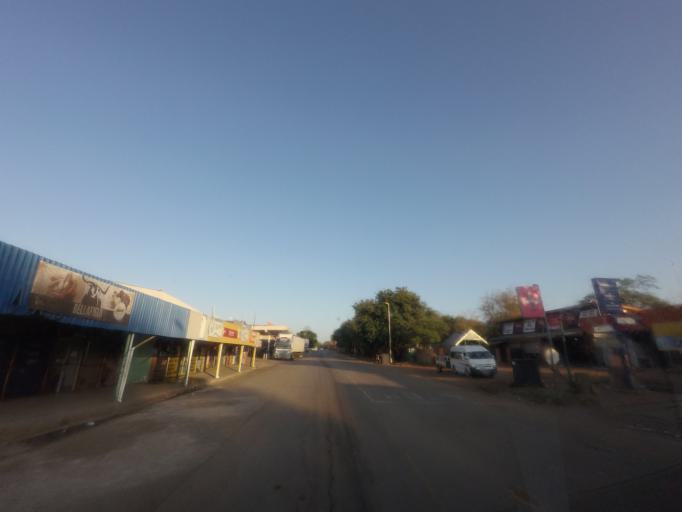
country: ZA
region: Mpumalanga
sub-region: Ehlanzeni District
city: Komatipoort
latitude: -25.4358
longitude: 31.9564
